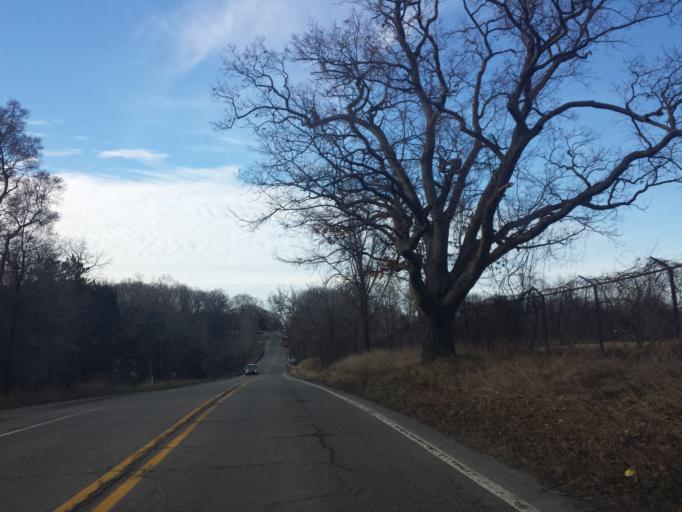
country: US
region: Michigan
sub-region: Oakland County
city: Rochester Hills
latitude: 42.6681
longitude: -83.1934
